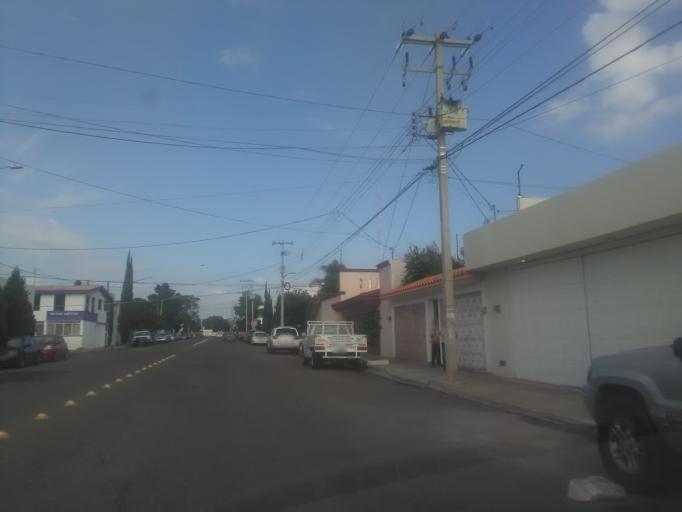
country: MX
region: Durango
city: Victoria de Durango
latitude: 24.0274
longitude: -104.6500
